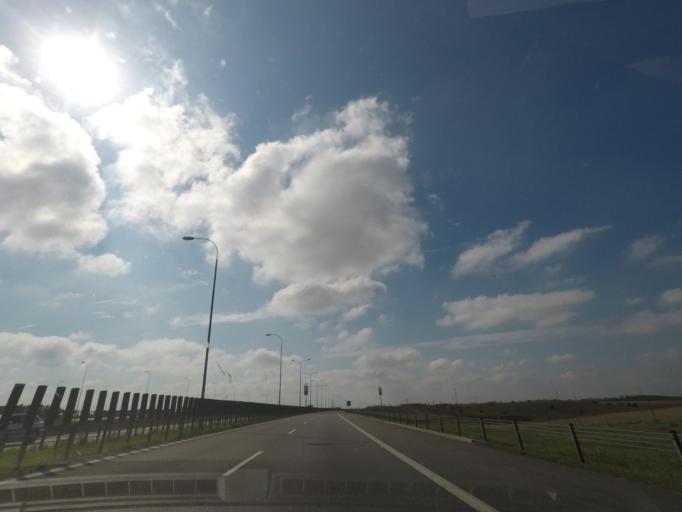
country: PL
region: Kujawsko-Pomorskie
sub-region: Powiat chelminski
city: Lisewo
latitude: 53.3488
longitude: 18.7071
